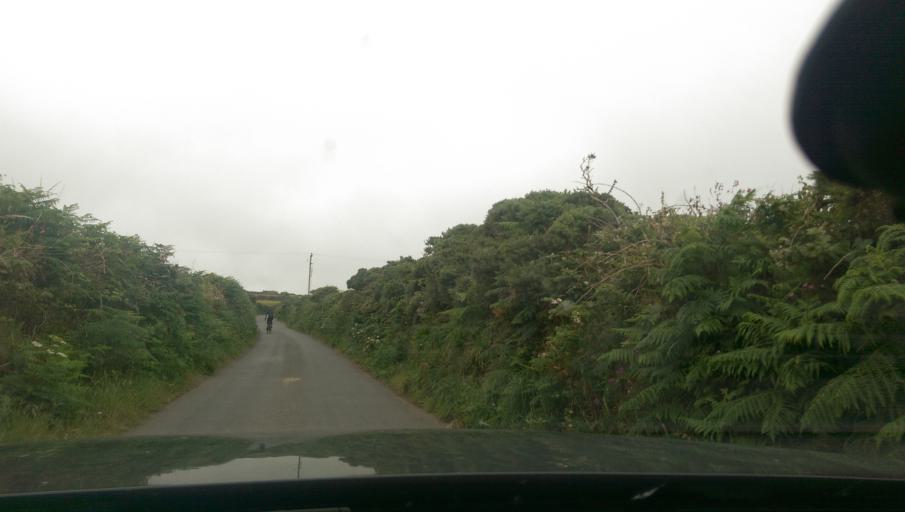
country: GB
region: England
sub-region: Cornwall
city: St. Buryan
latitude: 50.0950
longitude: -5.6478
